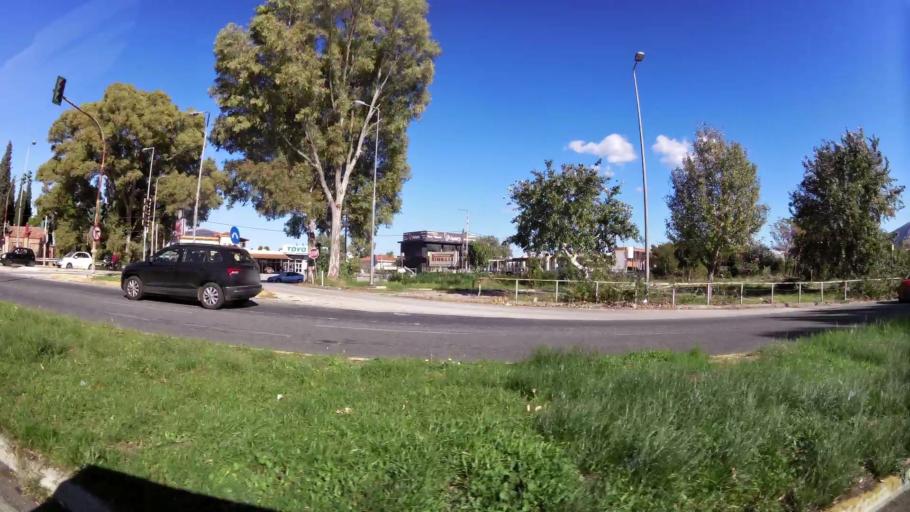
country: GR
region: Attica
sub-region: Nomarchia Anatolikis Attikis
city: Markopoulo
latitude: 37.8863
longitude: 23.9240
